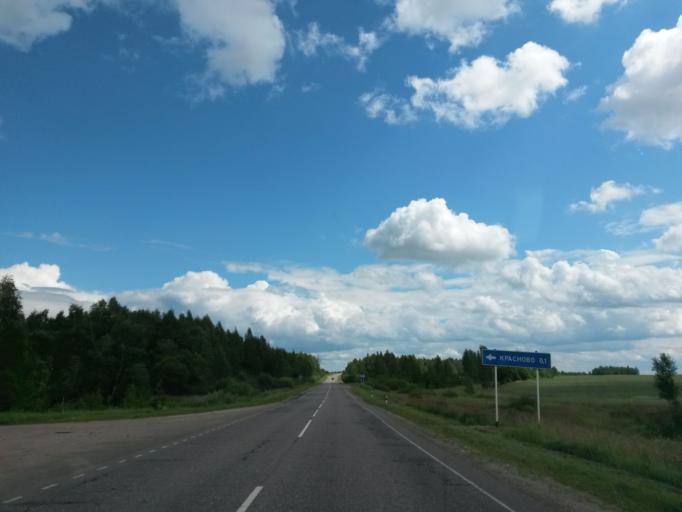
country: RU
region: Ivanovo
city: Pistsovo
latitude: 57.1881
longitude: 40.4412
